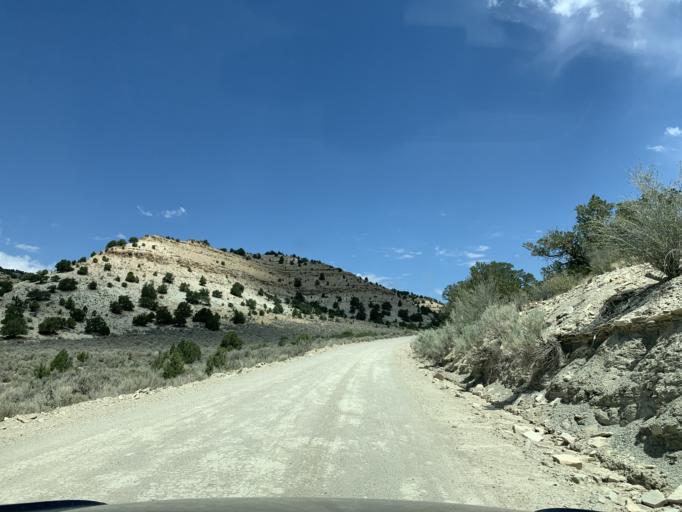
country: US
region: Utah
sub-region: Duchesne County
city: Duchesne
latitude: 39.8674
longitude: -110.2494
